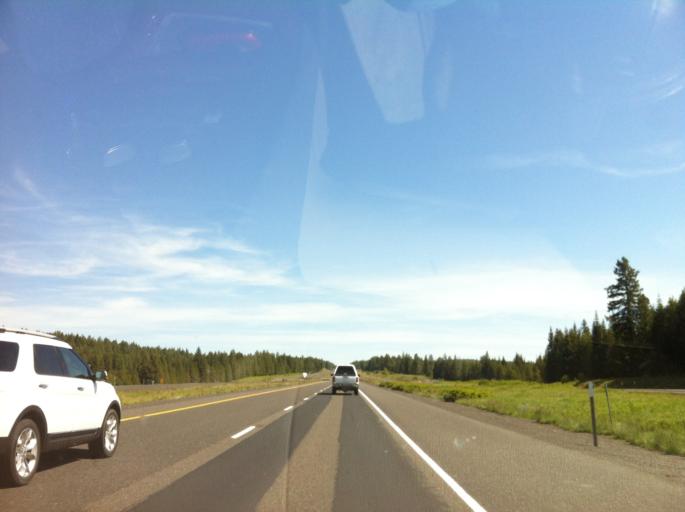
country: US
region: Oregon
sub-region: Umatilla County
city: Mission
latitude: 45.5104
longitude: -118.4298
